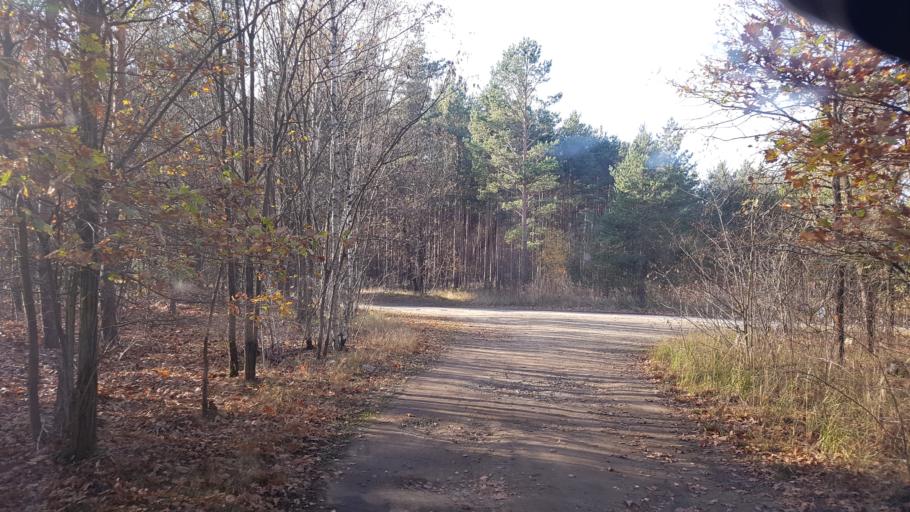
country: DE
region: Brandenburg
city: Grossraschen
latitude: 51.5983
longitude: 13.9924
